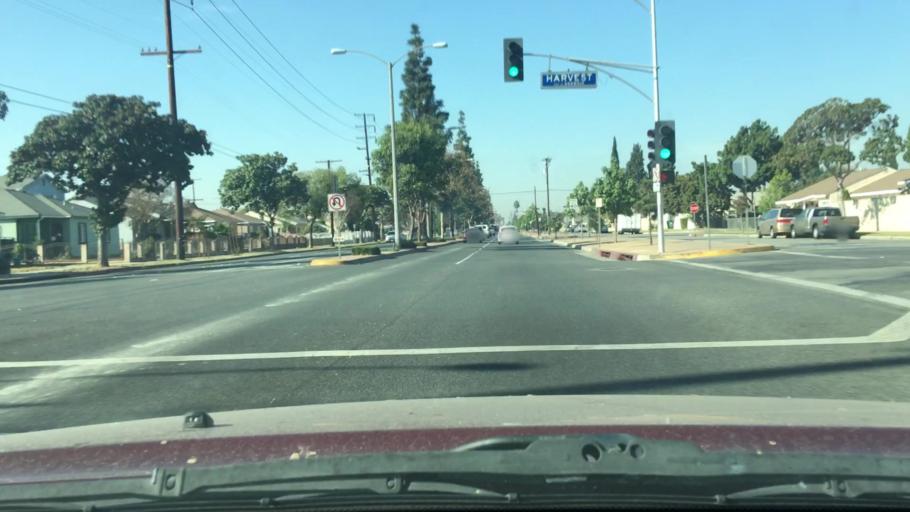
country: US
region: California
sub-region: Los Angeles County
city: Norwalk
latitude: 33.9022
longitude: -118.0922
